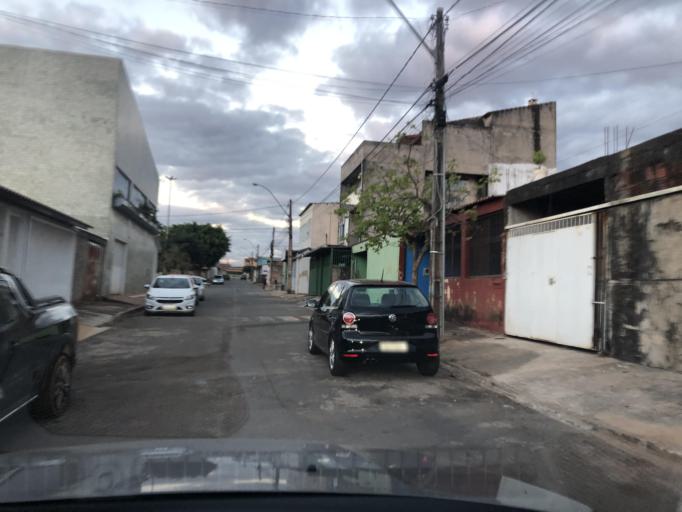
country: BR
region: Federal District
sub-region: Brasilia
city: Brasilia
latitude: -15.8778
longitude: -48.0980
